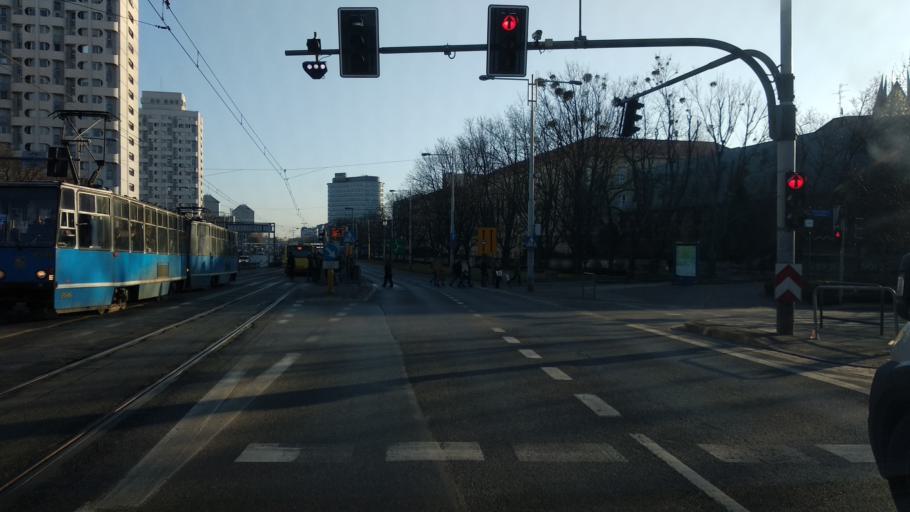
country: PL
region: Lower Silesian Voivodeship
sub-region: Powiat wroclawski
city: Wroclaw
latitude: 51.1101
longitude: 17.0544
